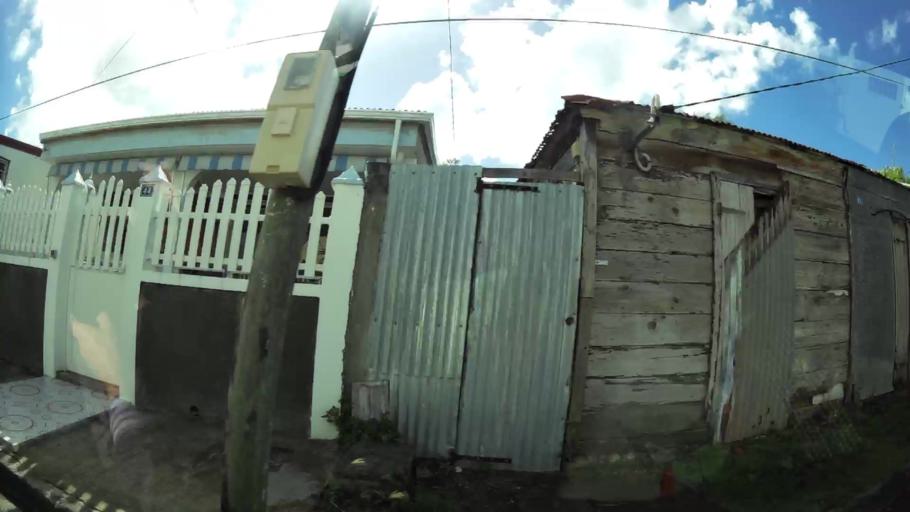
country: GP
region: Guadeloupe
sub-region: Guadeloupe
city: Port-Louis
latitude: 16.4192
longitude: -61.5307
